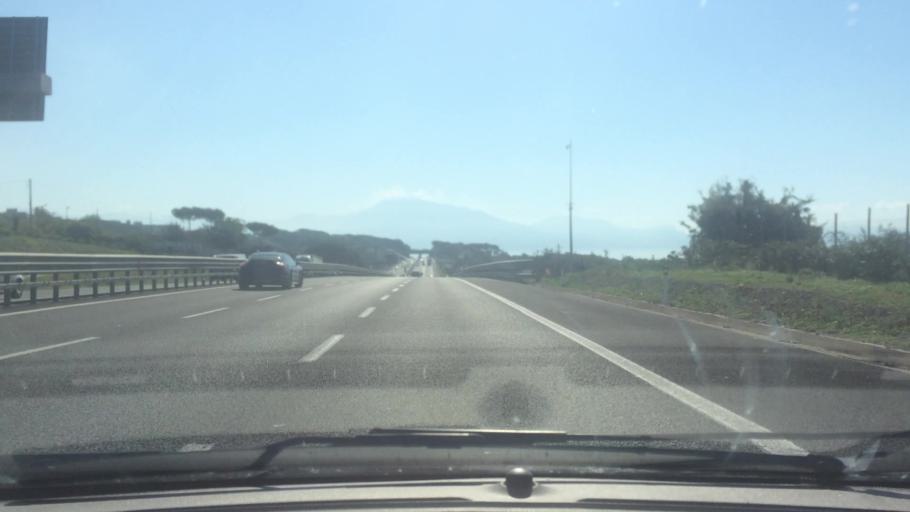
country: IT
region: Campania
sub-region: Provincia di Napoli
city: Ercolano
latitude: 40.8048
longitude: 14.3665
